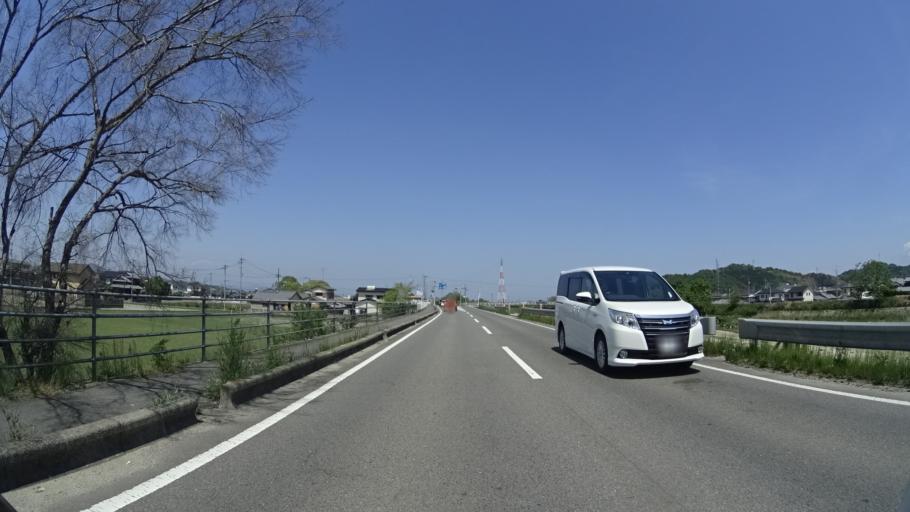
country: JP
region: Ehime
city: Hojo
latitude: 34.0316
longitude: 132.9672
